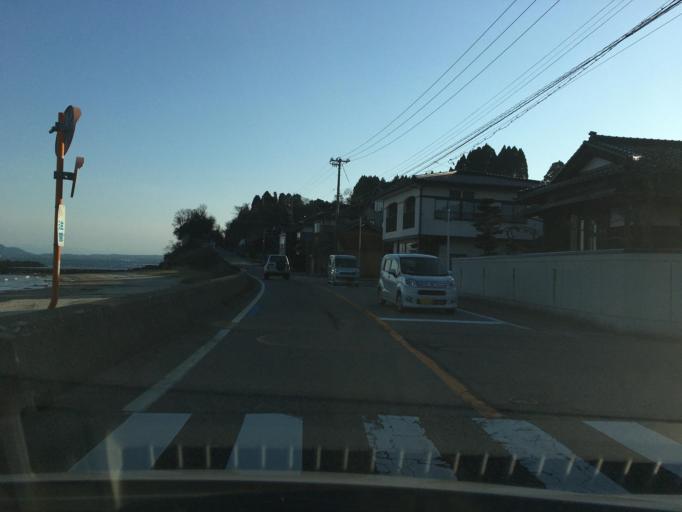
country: JP
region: Toyama
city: Himi
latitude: 36.9114
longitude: 137.0180
